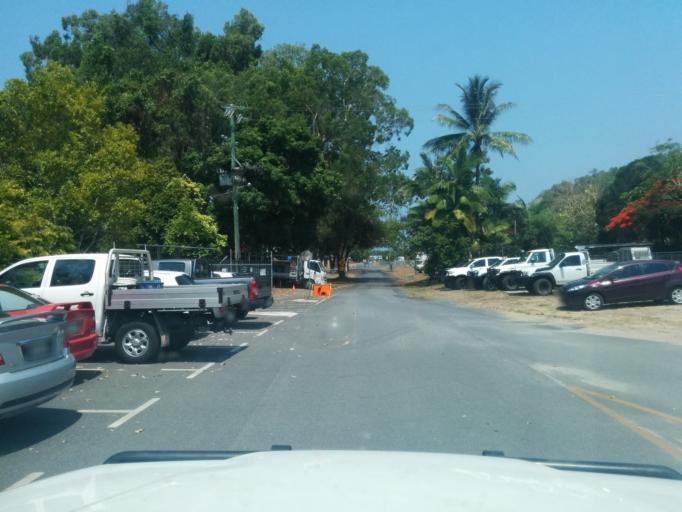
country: AU
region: Queensland
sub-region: Cairns
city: Redlynch
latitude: -16.8749
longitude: 145.7326
